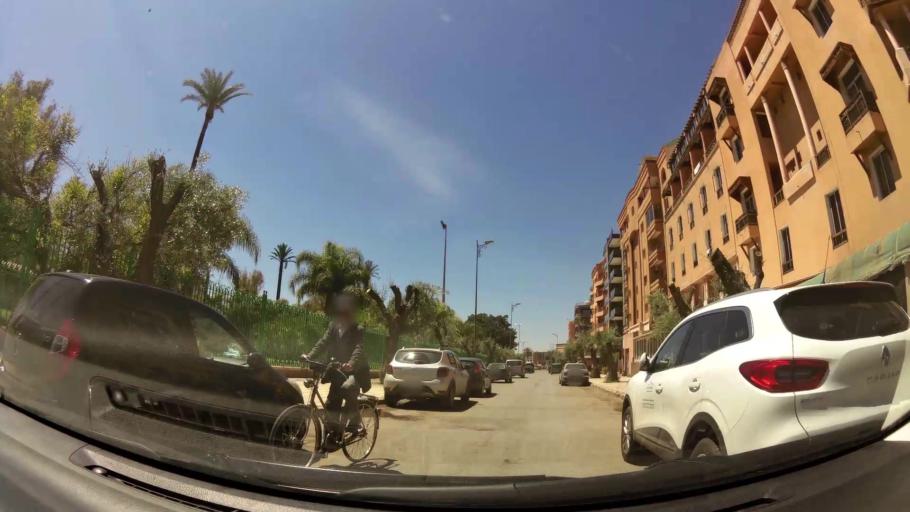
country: MA
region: Marrakech-Tensift-Al Haouz
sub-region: Marrakech
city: Marrakesh
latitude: 31.6307
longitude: -8.0111
